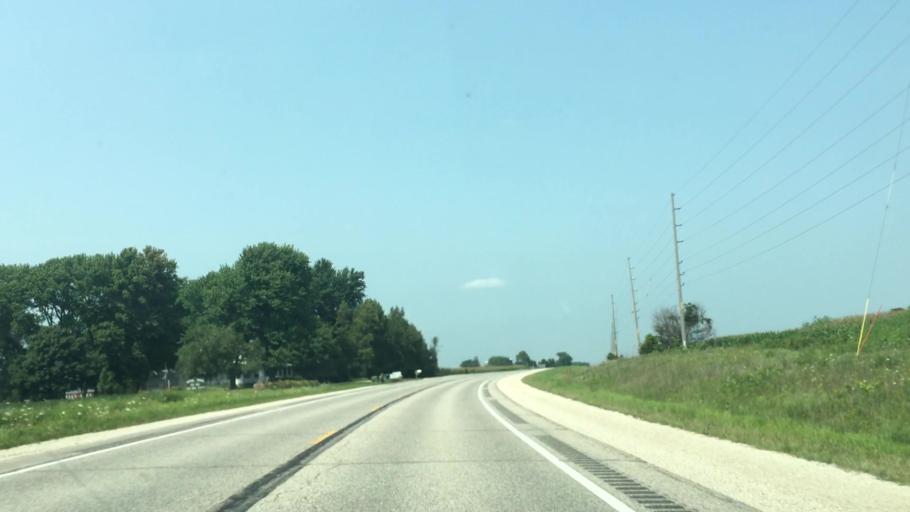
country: US
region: Iowa
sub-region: Fayette County
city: West Union
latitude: 42.9110
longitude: -91.8142
